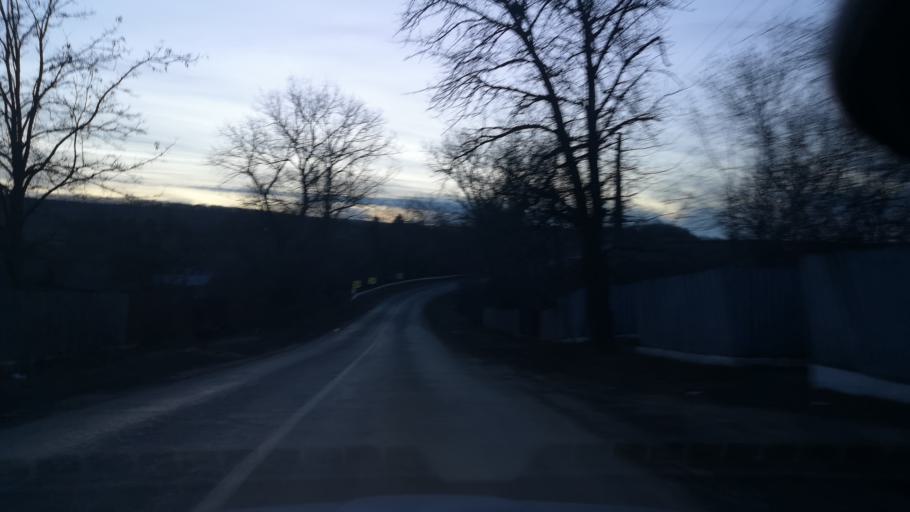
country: MD
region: Orhei
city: Orhei
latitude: 47.2840
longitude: 28.8449
